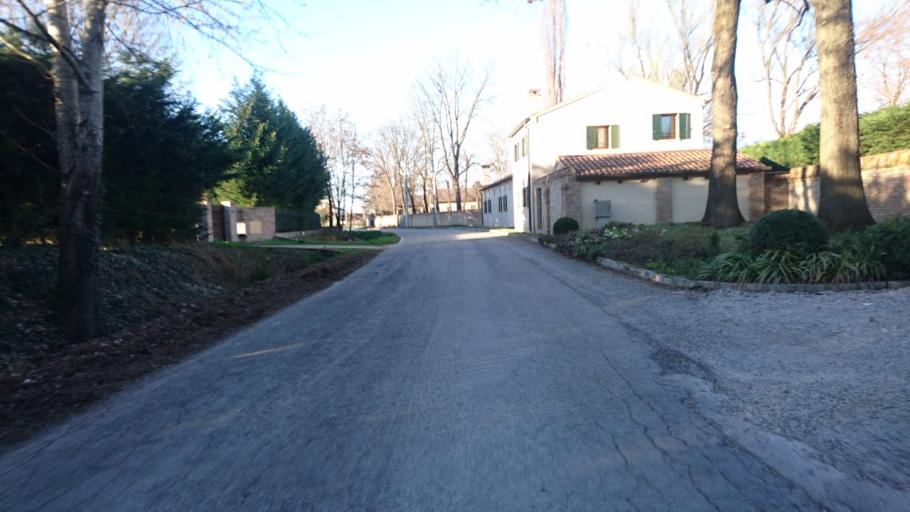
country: IT
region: Veneto
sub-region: Provincia di Padova
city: Bertipaglia
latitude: 45.3041
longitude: 11.8847
